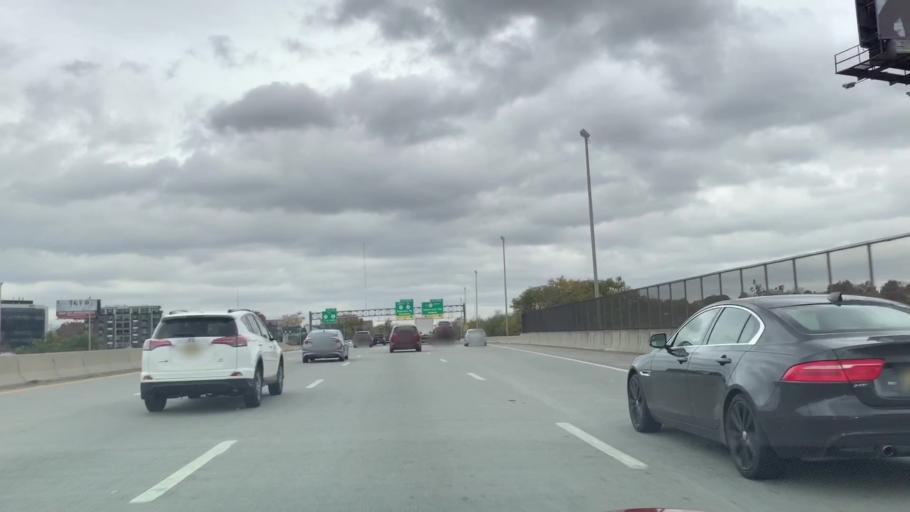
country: US
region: New Jersey
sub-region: Bergen County
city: Hackensack
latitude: 40.8708
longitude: -74.0578
